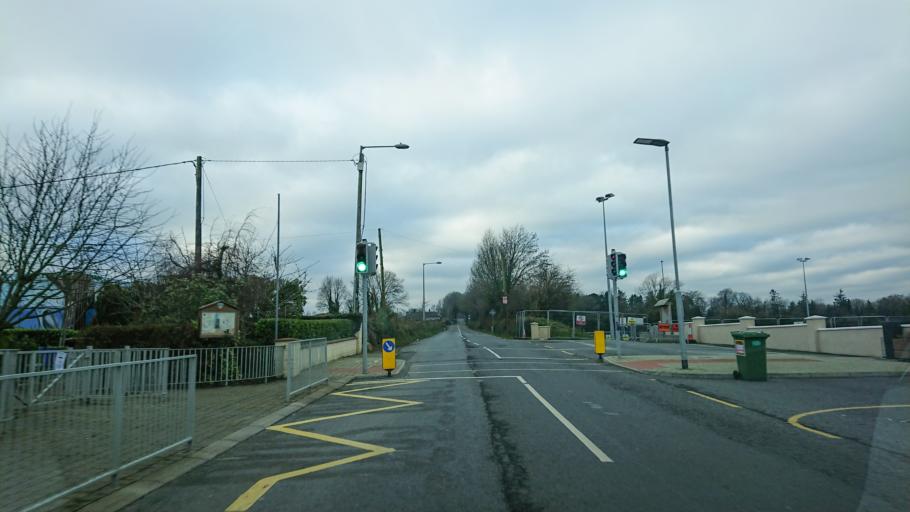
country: IE
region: Munster
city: Carrick-on-Suir
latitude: 52.3064
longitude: -7.4994
